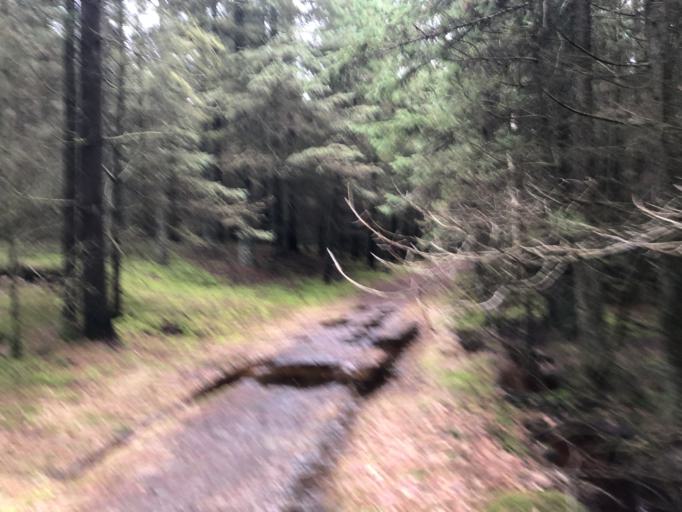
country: DK
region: Central Jutland
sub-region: Holstebro Kommune
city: Ulfborg
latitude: 56.2883
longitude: 8.1790
